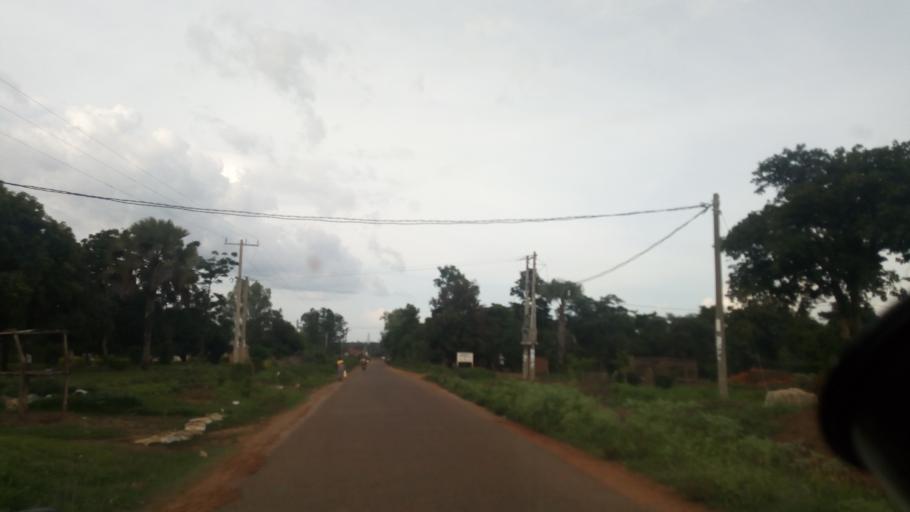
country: UG
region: Northern Region
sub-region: Lira District
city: Lira
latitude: 2.2599
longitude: 32.8568
